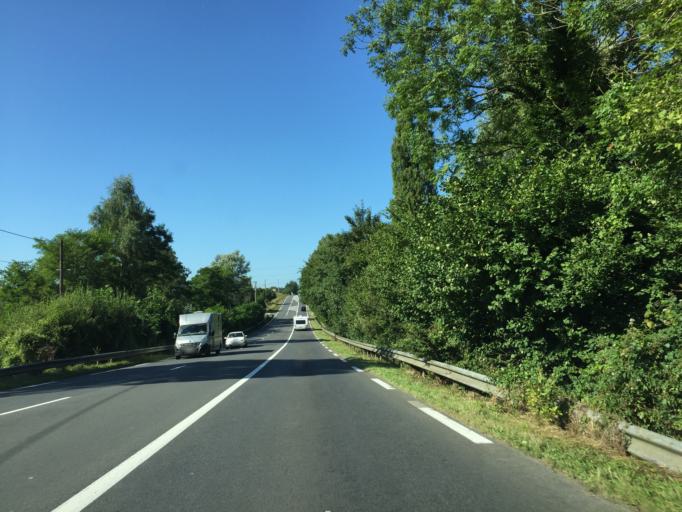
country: FR
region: Lower Normandy
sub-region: Departement du Calvados
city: Lisieux
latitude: 49.2025
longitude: 0.2268
